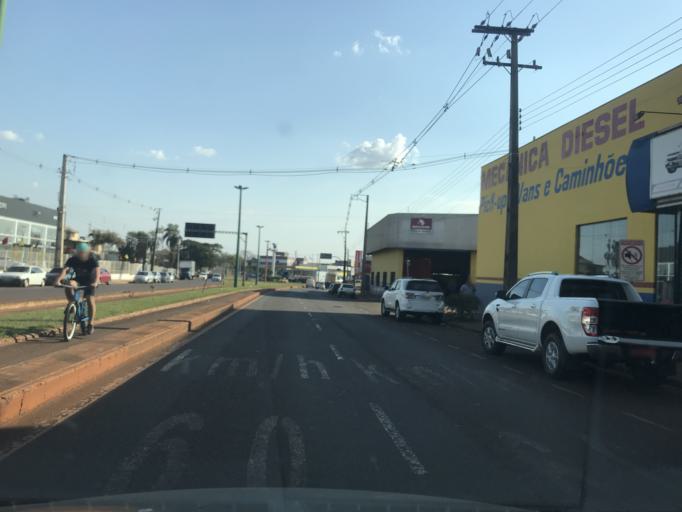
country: BR
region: Parana
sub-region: Toledo
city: Toledo
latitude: -24.7194
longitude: -53.7144
